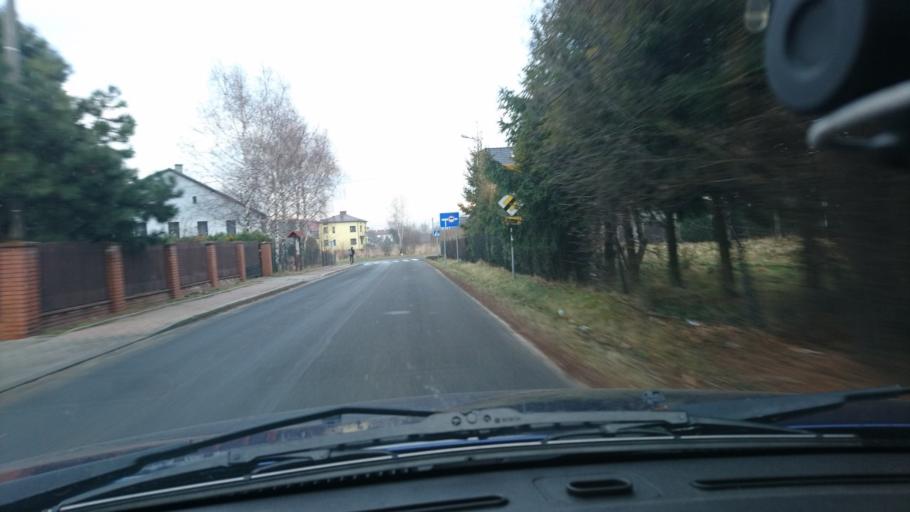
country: PL
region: Silesian Voivodeship
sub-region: Powiat bielski
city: Buczkowice
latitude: 49.7266
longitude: 19.0658
